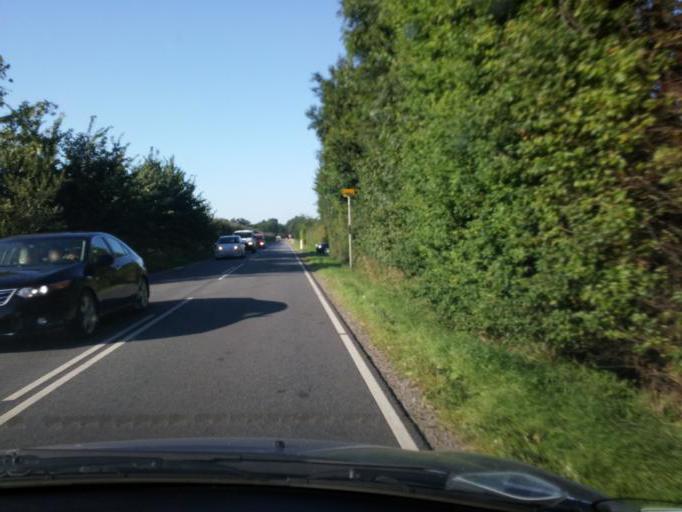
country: DK
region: South Denmark
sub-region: Kerteminde Kommune
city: Langeskov
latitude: 55.4016
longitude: 10.5555
